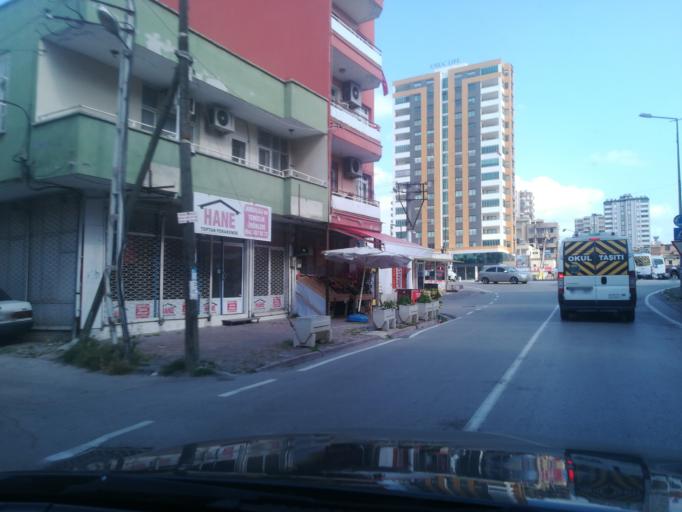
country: TR
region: Adana
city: Adana
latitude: 37.0089
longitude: 35.3209
